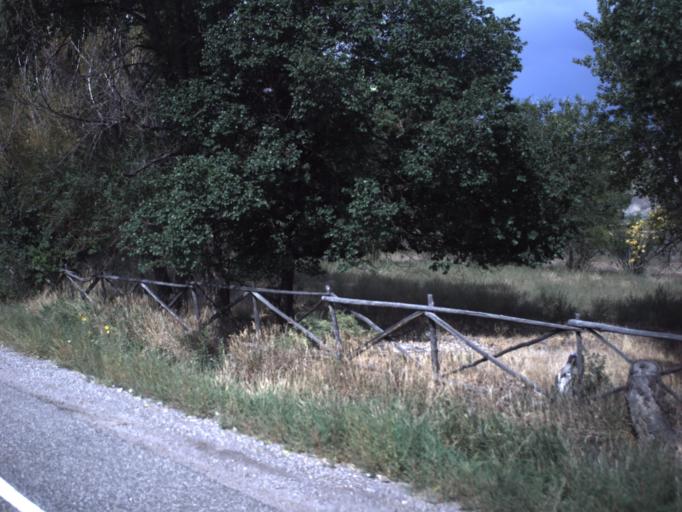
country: US
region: Utah
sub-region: Sevier County
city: Monroe
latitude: 38.4524
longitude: -112.2305
